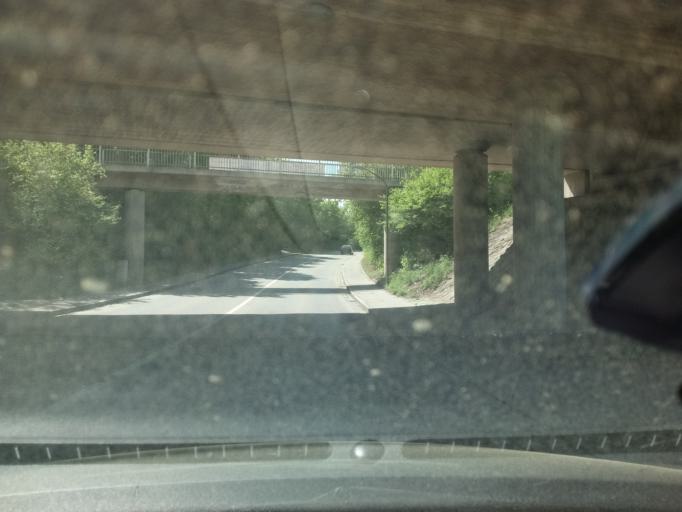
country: DE
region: Bavaria
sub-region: Upper Bavaria
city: Ampfing
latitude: 48.2538
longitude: 12.4177
